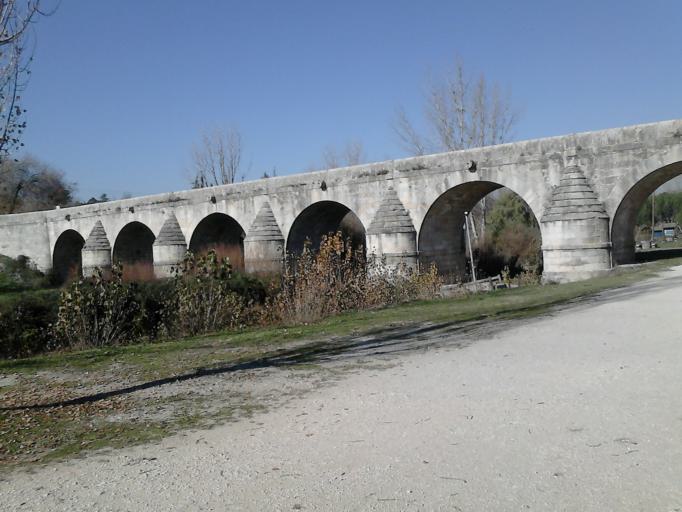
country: ES
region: Madrid
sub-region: Provincia de Madrid
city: Villanueva del Pardillo
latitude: 40.5190
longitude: -3.9392
